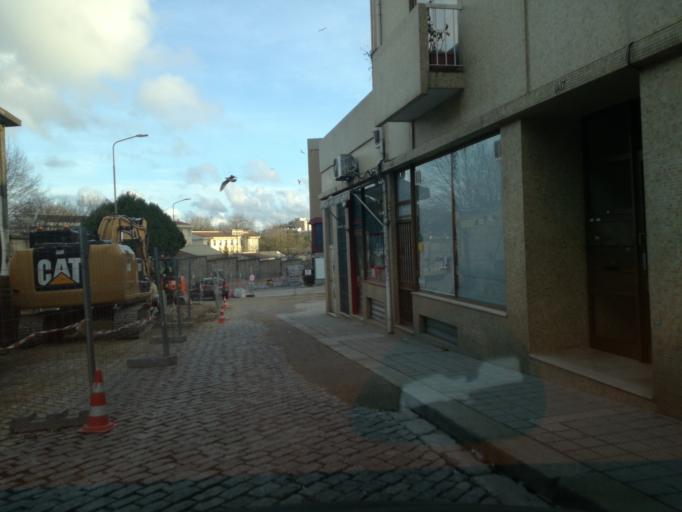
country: PT
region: Porto
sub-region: Porto
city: Porto
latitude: 41.1595
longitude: -8.6206
